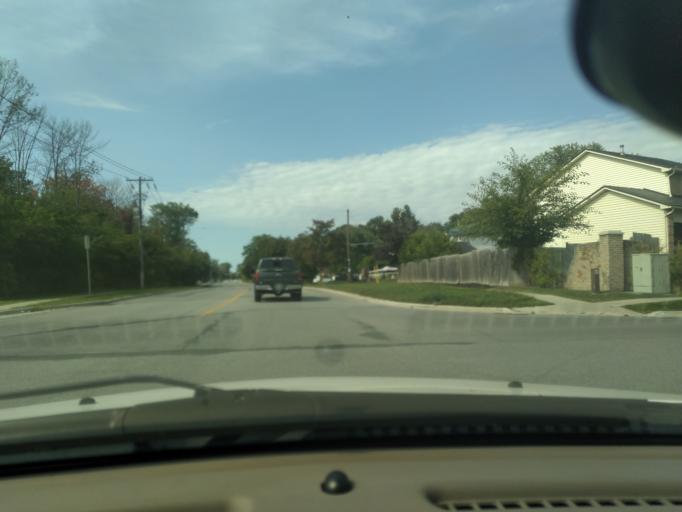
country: CA
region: Ontario
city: Barrie
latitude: 44.3828
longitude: -79.7184
